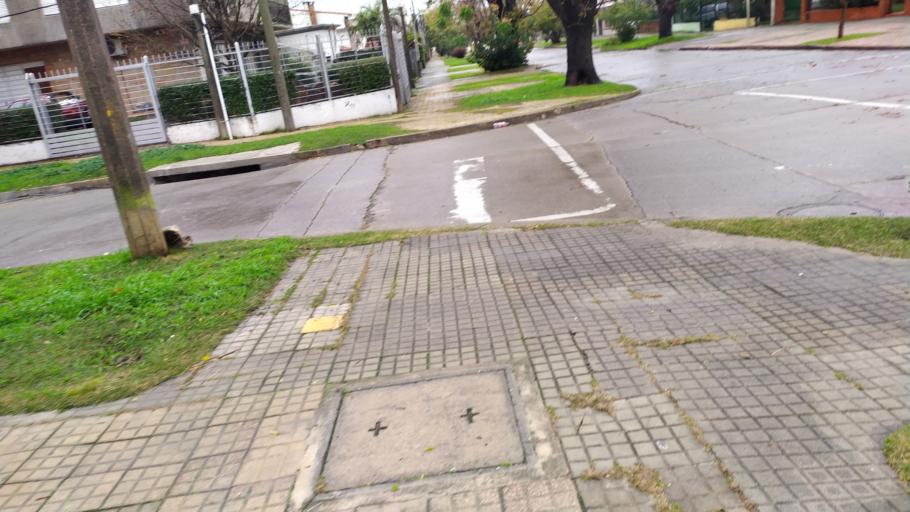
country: UY
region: Canelones
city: Paso de Carrasco
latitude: -34.8929
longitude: -56.1008
